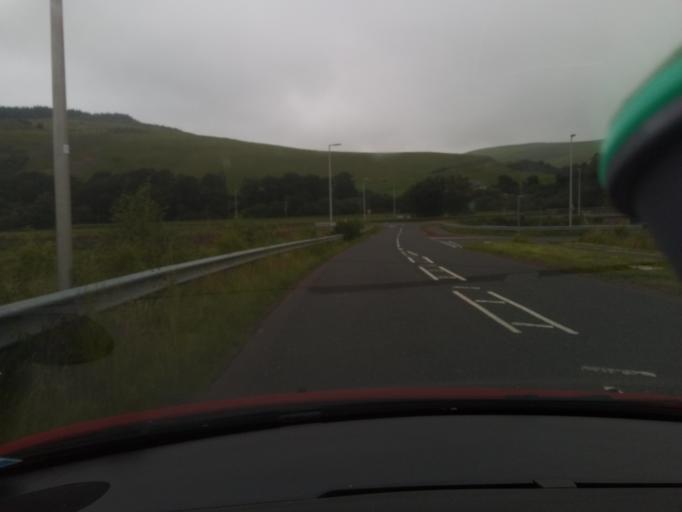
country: GB
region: Scotland
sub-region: Fife
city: Pathhead
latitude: 55.7397
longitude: -2.9143
